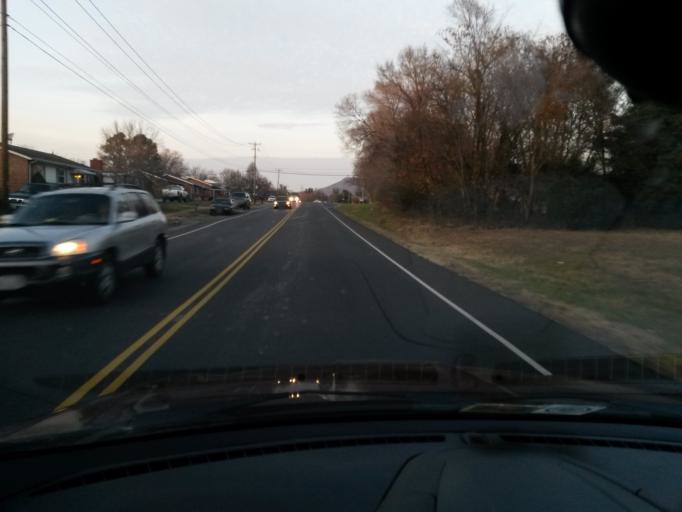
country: US
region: Virginia
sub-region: Roanoke County
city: Hollins
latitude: 37.3272
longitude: -79.9372
